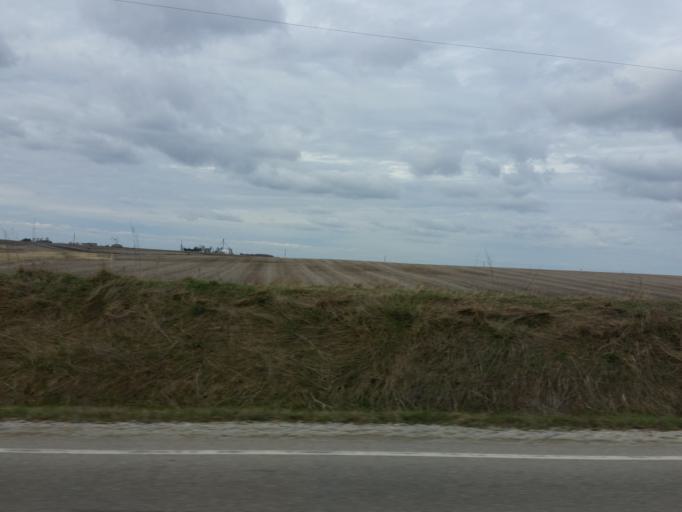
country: US
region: Iowa
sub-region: Black Hawk County
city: Elk Run Heights
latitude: 42.5704
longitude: -92.2315
